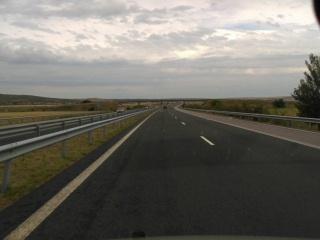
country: BG
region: Sliven
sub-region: Obshtina Sliven
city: Kermen
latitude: 42.5043
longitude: 26.3106
